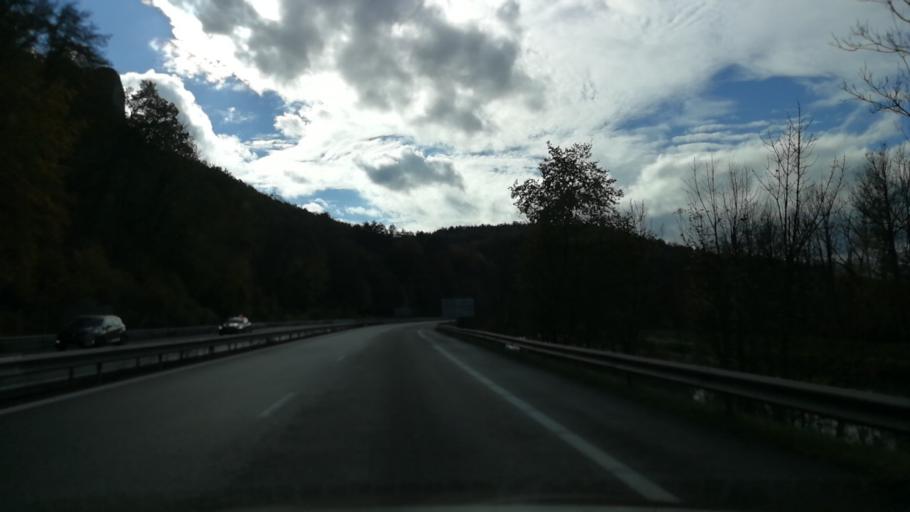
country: FR
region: Bourgogne
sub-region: Departement de la Cote-d'Or
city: Velars-sur-Ouche
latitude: 47.3215
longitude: 4.9316
